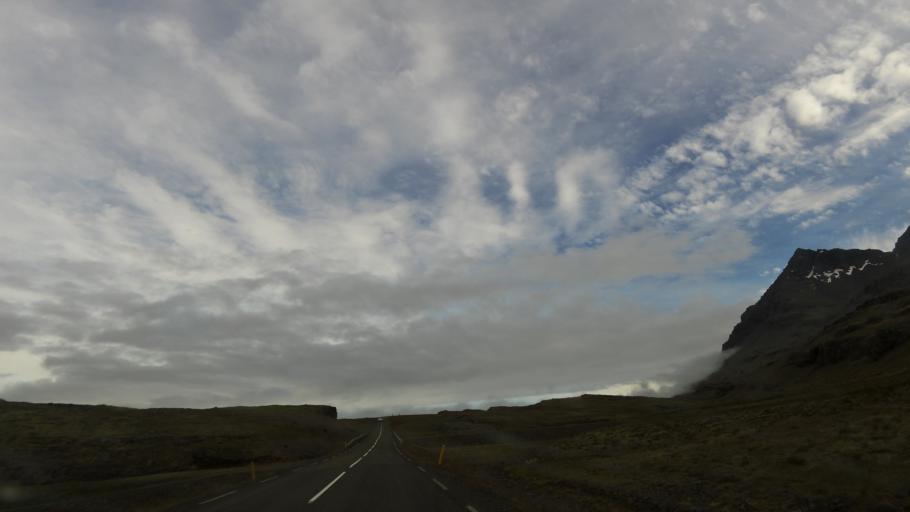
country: IS
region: East
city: Reydarfjoerdur
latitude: 64.7289
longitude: -14.4116
